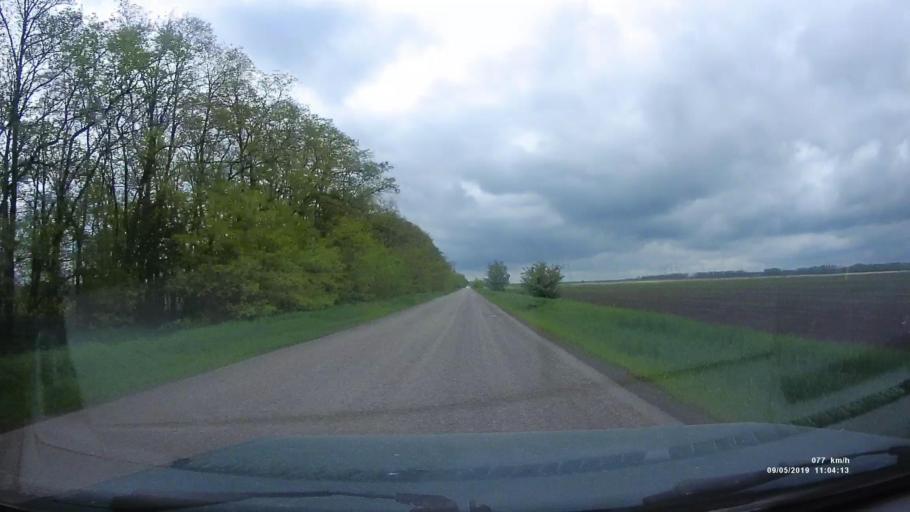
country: RU
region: Krasnodarskiy
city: Kanelovskaya
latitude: 46.8197
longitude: 39.2100
